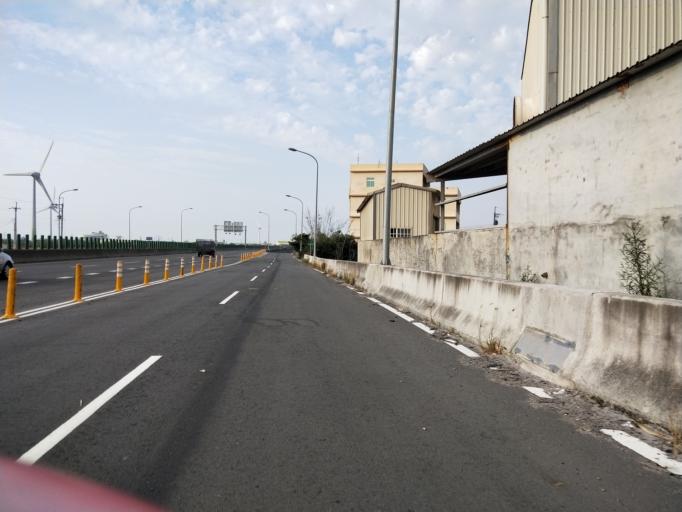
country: TW
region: Taiwan
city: Fengyuan
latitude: 24.3659
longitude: 120.5859
